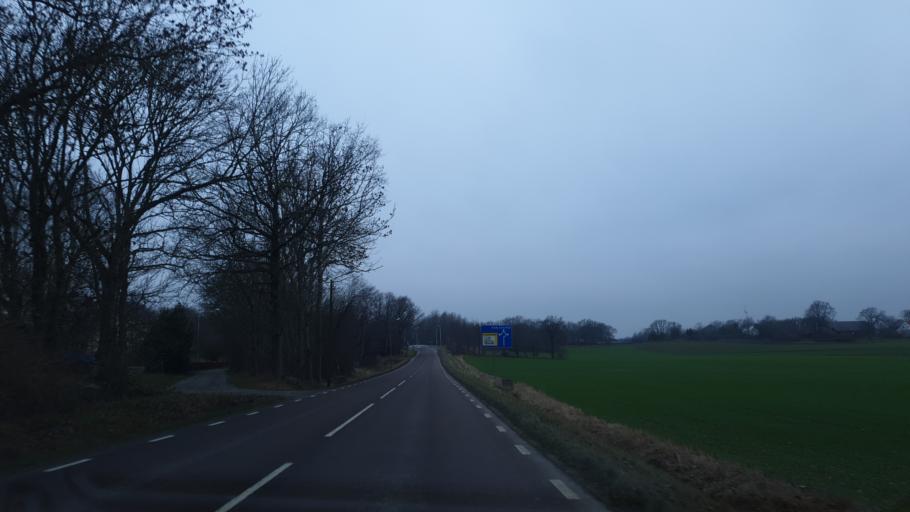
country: SE
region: Blekinge
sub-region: Karlskrona Kommun
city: Jaemjoe
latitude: 56.1682
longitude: 15.7454
